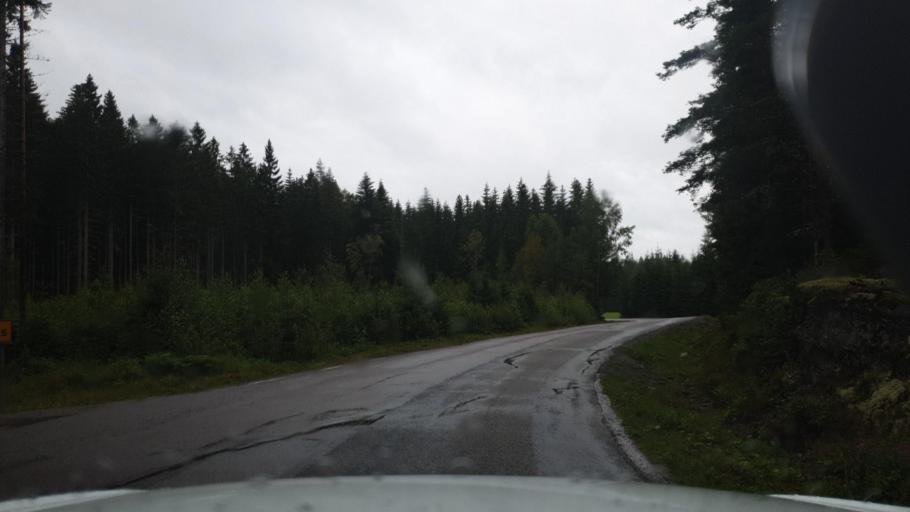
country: SE
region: Vaermland
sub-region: Grums Kommun
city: Slottsbron
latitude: 59.4944
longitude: 12.8781
